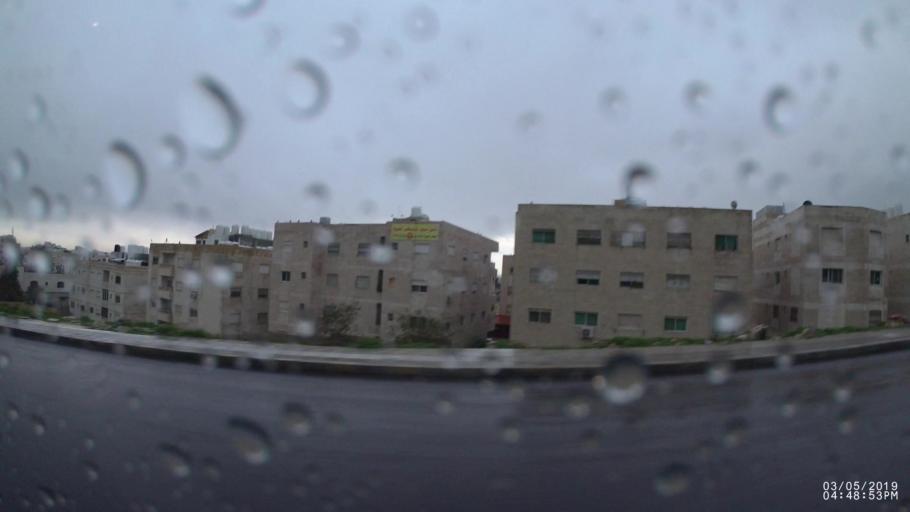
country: JO
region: Amman
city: Amman
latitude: 32.0020
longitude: 35.9599
